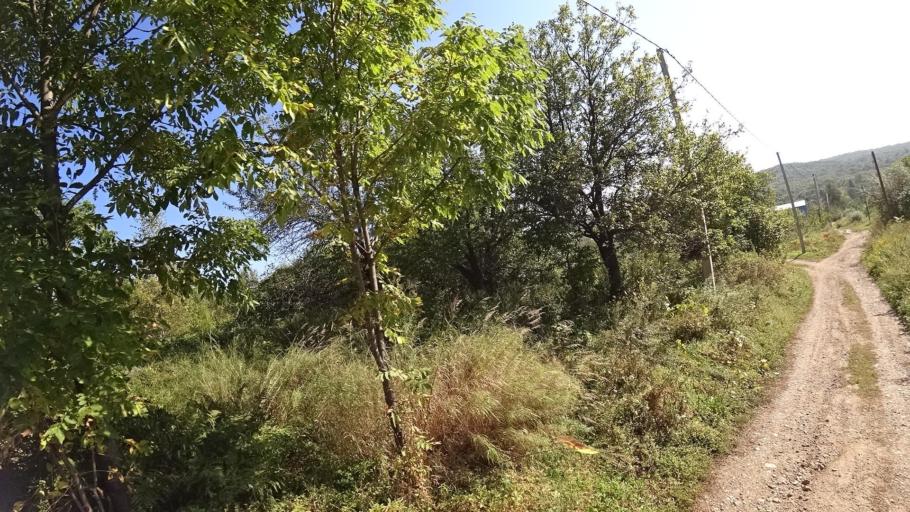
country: RU
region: Jewish Autonomous Oblast
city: Bira
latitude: 49.0095
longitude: 132.4739
